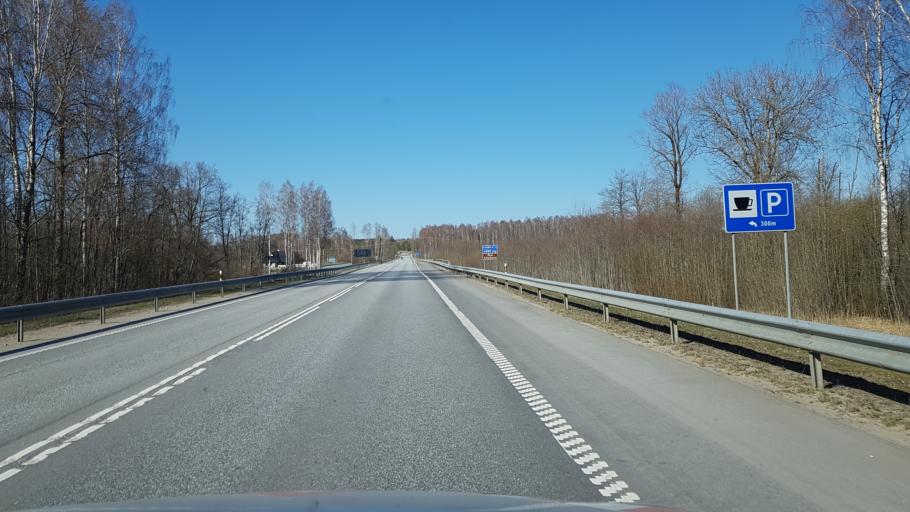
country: EE
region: Tartu
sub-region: Tartu linn
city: Tartu
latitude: 58.4642
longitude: 26.7859
